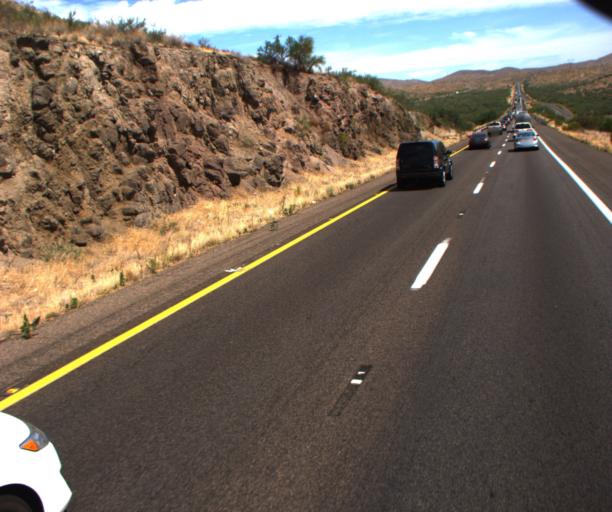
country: US
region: Arizona
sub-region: Yavapai County
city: Cordes Lakes
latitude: 34.2335
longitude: -112.1114
